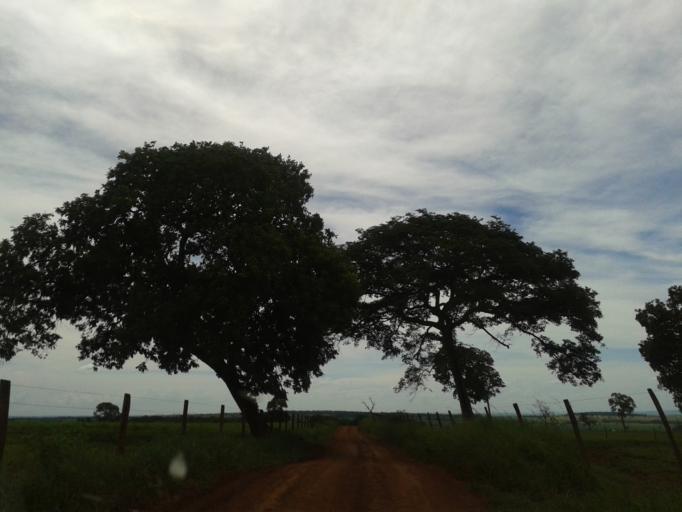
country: BR
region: Minas Gerais
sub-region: Capinopolis
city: Capinopolis
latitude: -18.7503
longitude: -49.8262
